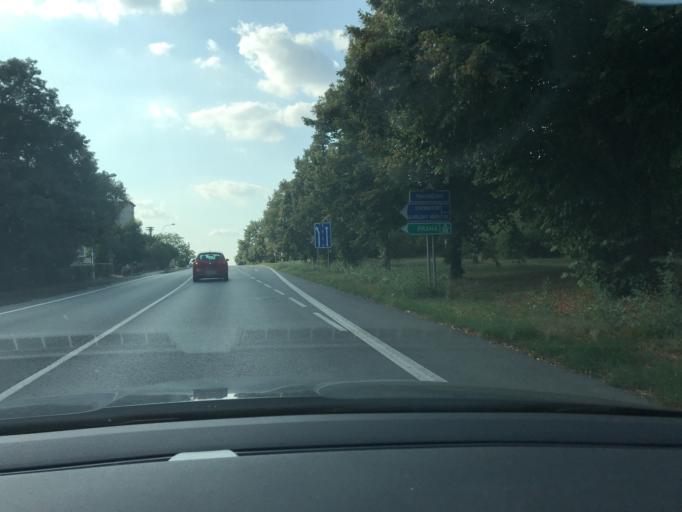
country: CZ
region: Central Bohemia
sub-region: Okres Kladno
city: Slany
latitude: 50.2348
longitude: 14.0765
